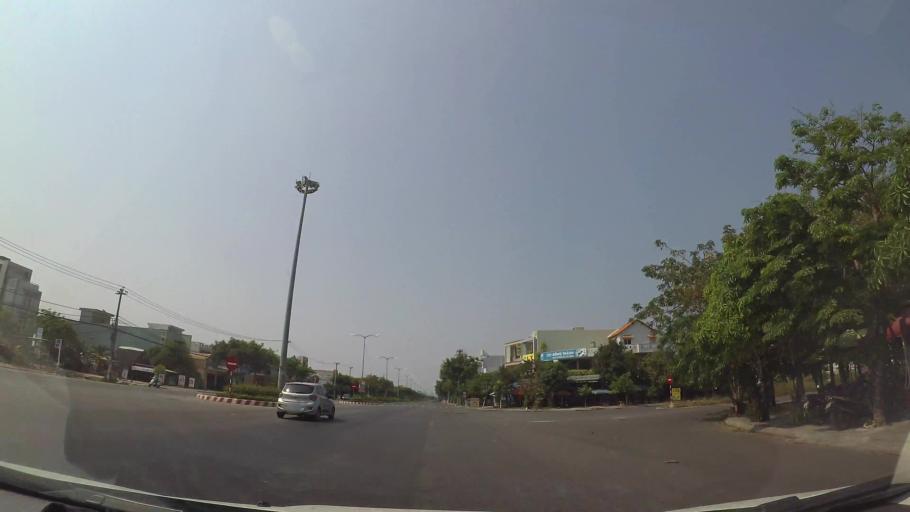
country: VN
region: Da Nang
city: Ngu Hanh Son
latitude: 16.0095
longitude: 108.2577
